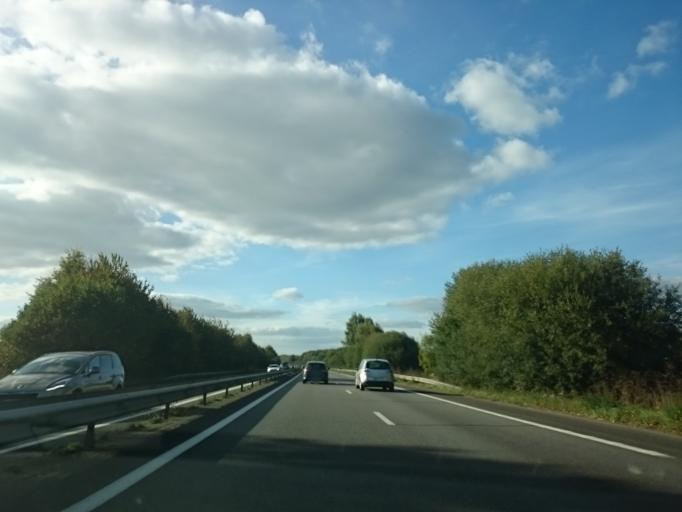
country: FR
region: Pays de la Loire
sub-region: Departement de la Loire-Atlantique
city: Orvault
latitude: 47.2930
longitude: -1.6135
